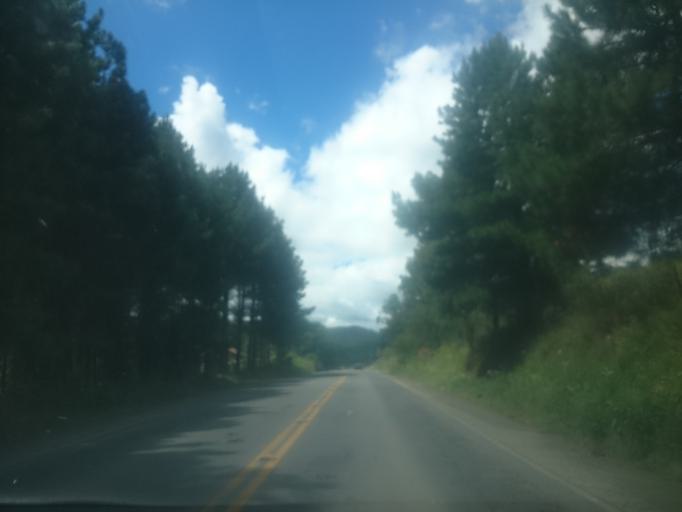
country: BR
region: Santa Catarina
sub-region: Correia Pinto
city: Correia Pinto
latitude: -27.6564
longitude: -50.1972
